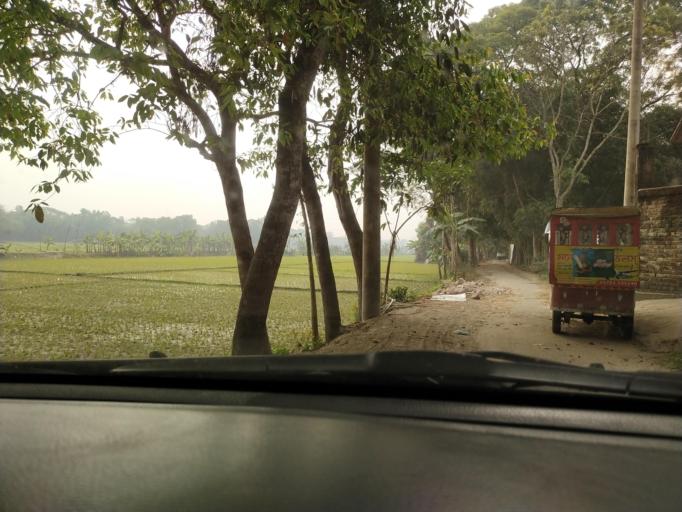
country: BD
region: Dhaka
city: Narsingdi
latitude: 24.0342
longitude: 90.7191
